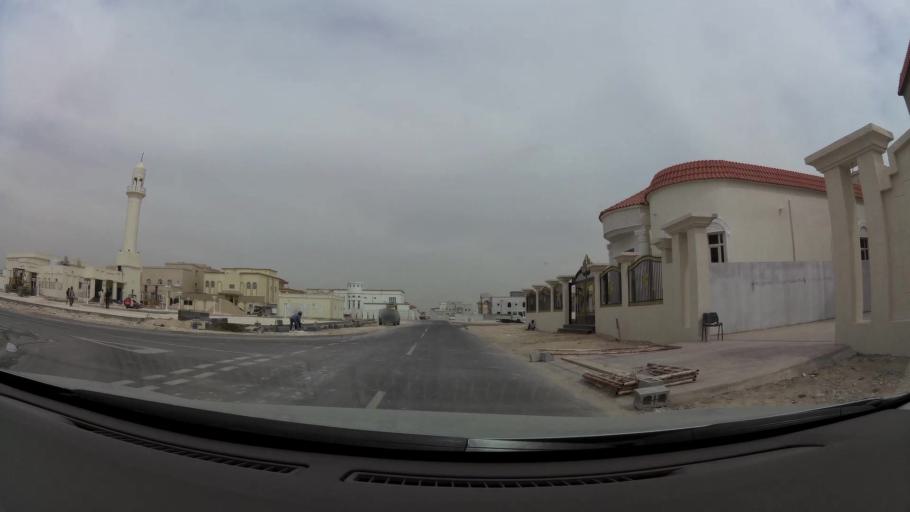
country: QA
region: Baladiyat ar Rayyan
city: Ar Rayyan
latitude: 25.2100
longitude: 51.4507
